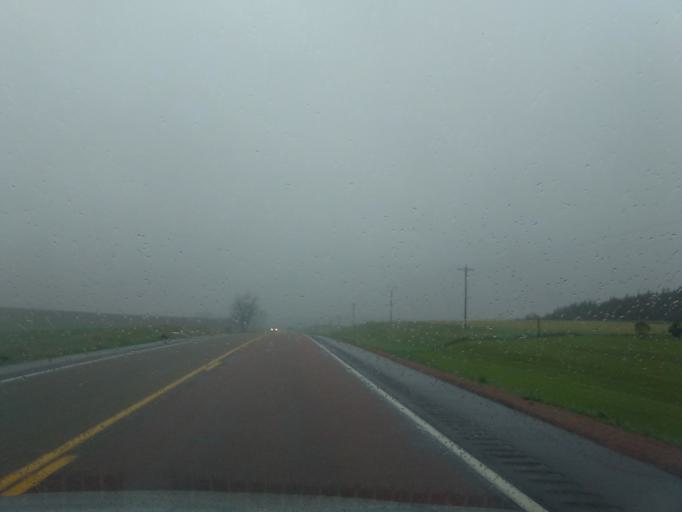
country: US
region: Nebraska
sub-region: Wayne County
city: Wayne
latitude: 42.2354
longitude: -97.0913
